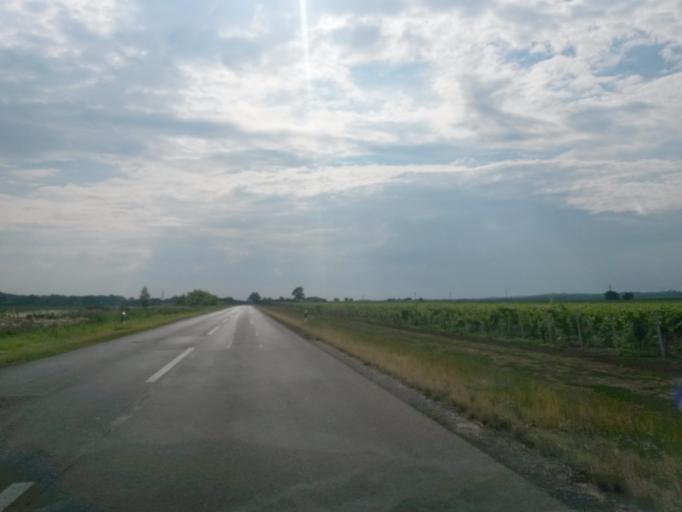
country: HR
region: Osjecko-Baranjska
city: Dalj
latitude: 45.5062
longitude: 19.0328
